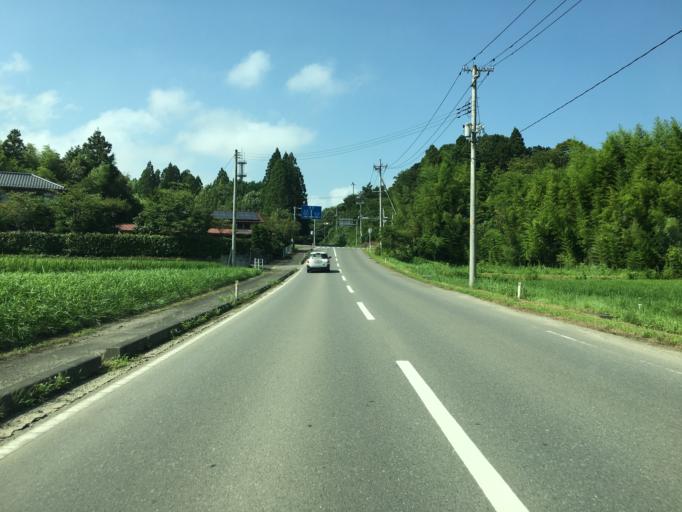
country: JP
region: Miyagi
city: Marumori
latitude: 37.8624
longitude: 140.8923
